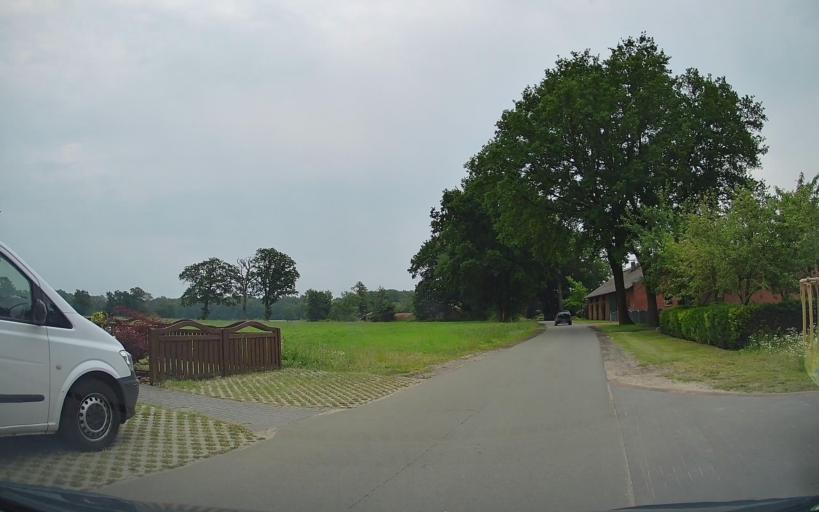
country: DE
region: Lower Saxony
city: Friesoythe
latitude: 53.0411
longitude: 7.8613
